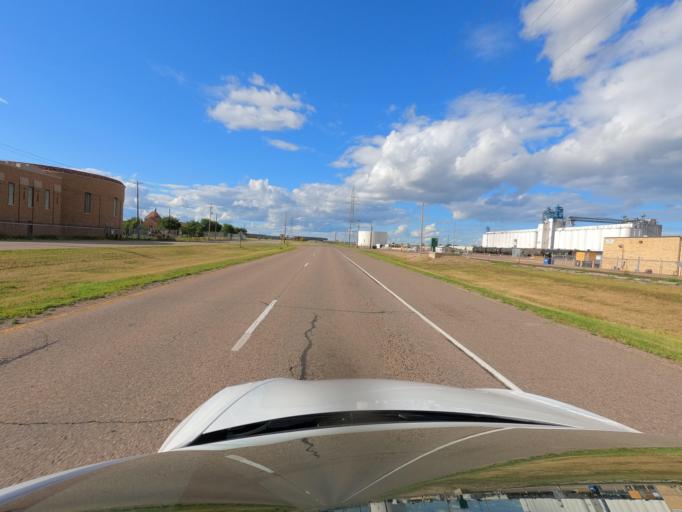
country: US
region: Minnesota
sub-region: Anoka County
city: Columbia Heights
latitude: 45.0456
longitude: -93.2750
